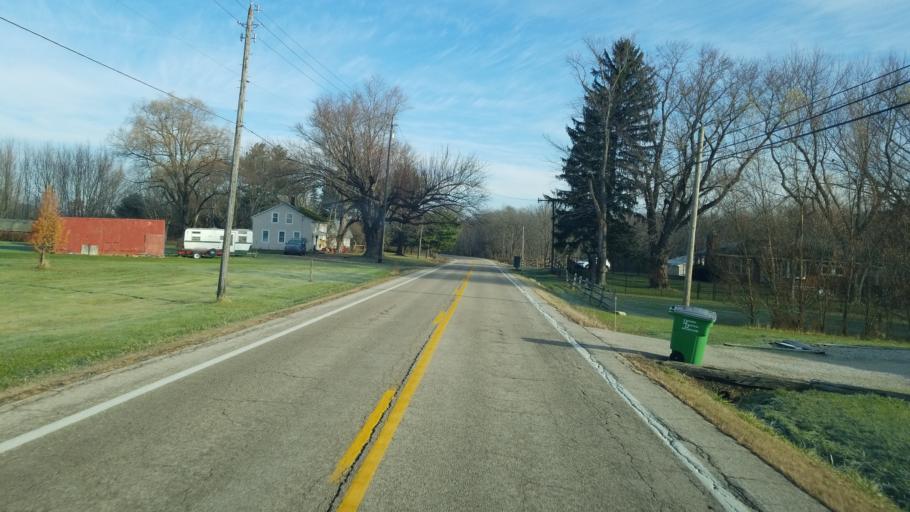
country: US
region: Ohio
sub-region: Ashtabula County
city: North Kingsville
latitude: 41.8126
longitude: -80.6660
